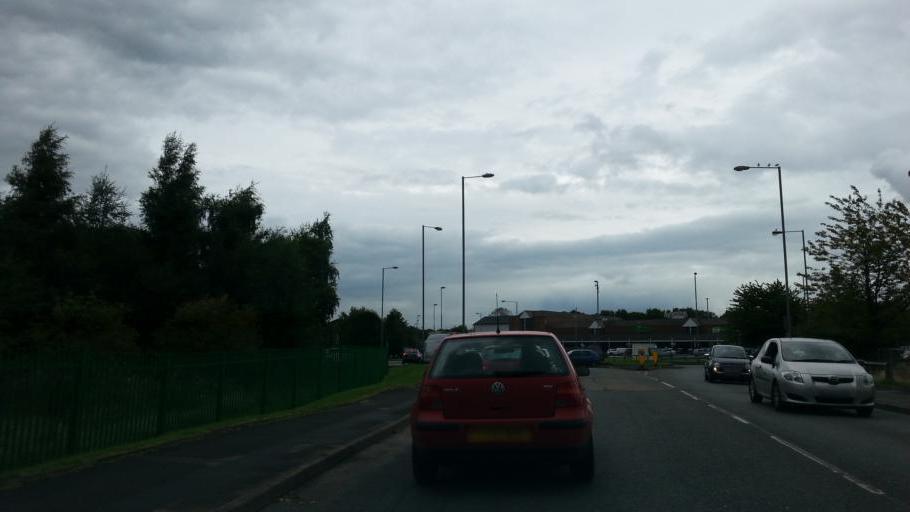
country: GB
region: England
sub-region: Borough of Bury
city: Bury
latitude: 53.5766
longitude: -2.2766
